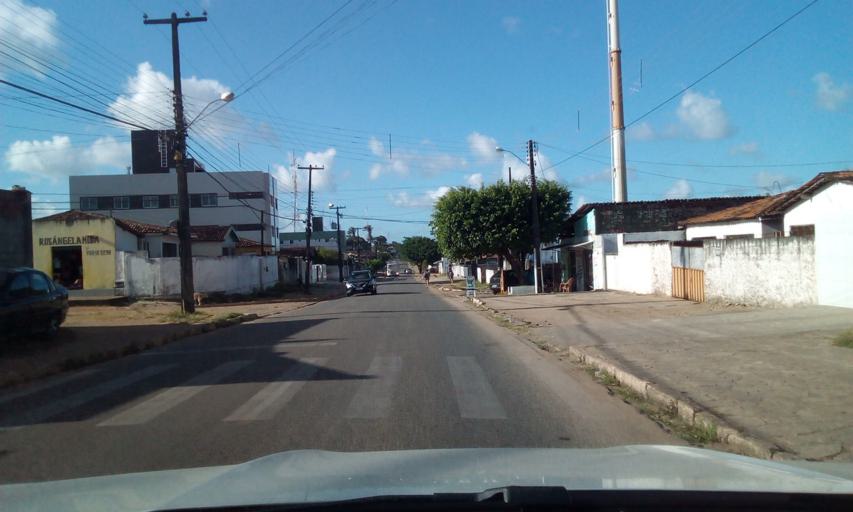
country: BR
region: Paraiba
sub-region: Bayeux
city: Bayeux
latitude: -7.1392
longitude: -34.9115
